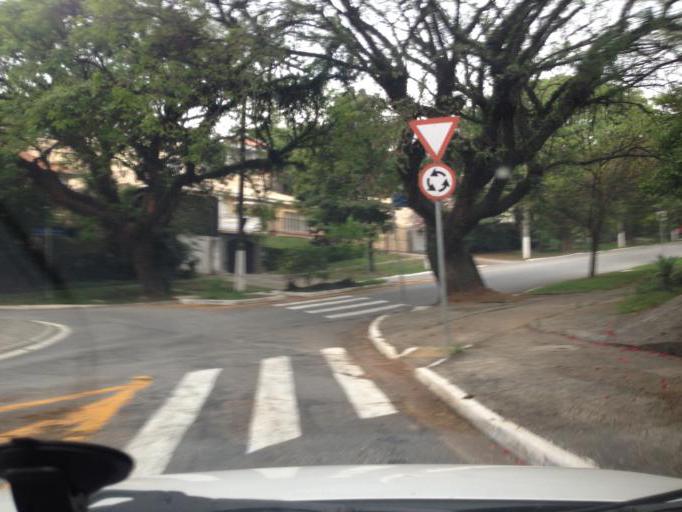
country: BR
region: Sao Paulo
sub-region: Osasco
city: Osasco
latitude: -23.5291
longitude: -46.7133
